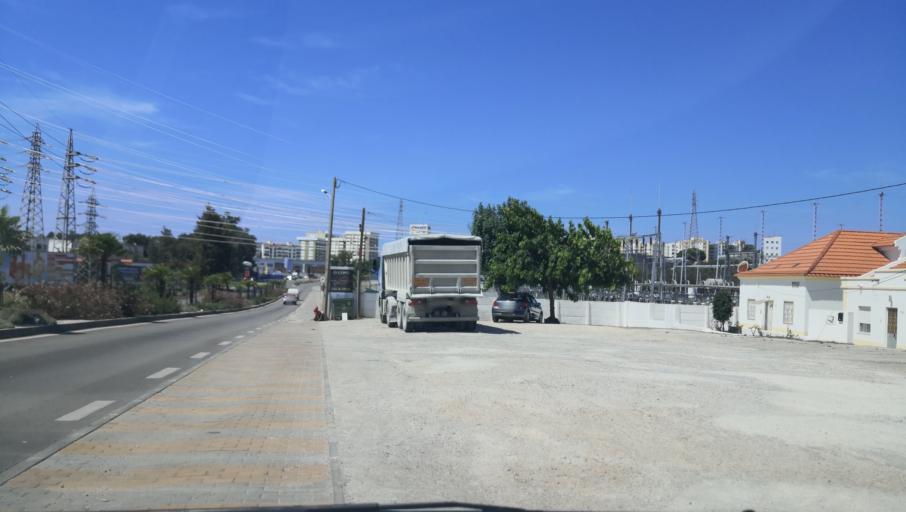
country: PT
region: Setubal
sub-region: Setubal
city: Setubal
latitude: 38.5363
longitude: -8.8604
